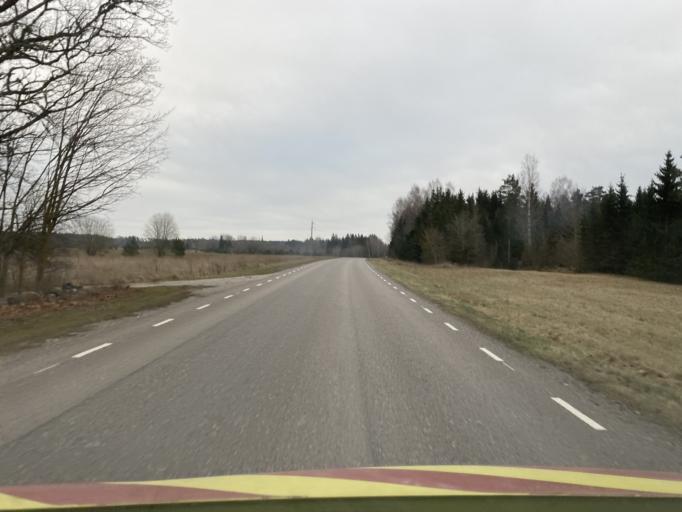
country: EE
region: Laeaene
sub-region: Ridala Parish
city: Uuemoisa
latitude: 59.0184
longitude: 23.6765
